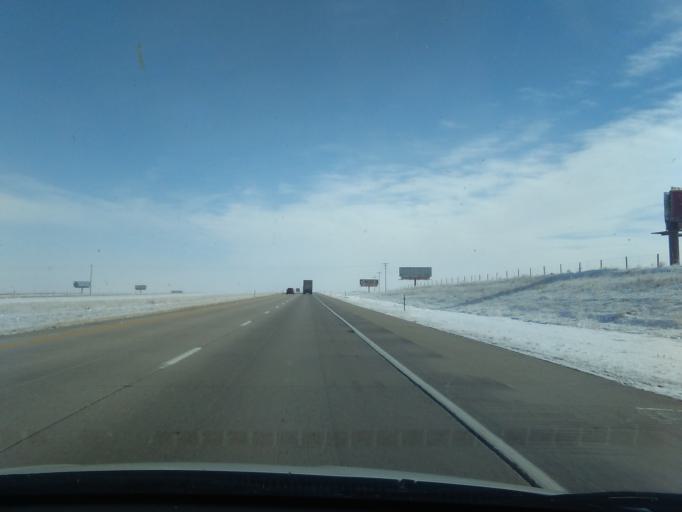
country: US
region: Wyoming
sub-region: Laramie County
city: Fox Farm-College
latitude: 41.1564
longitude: -104.4505
